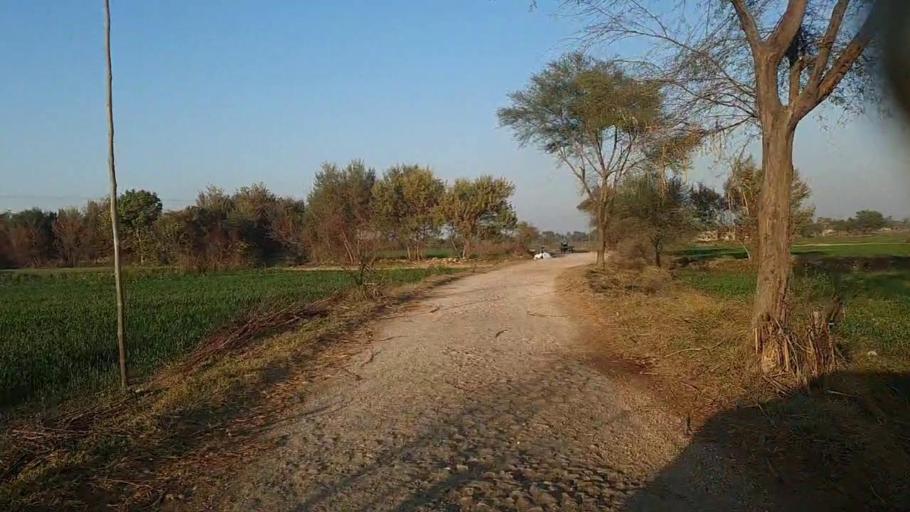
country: PK
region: Sindh
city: Mirpur Mathelo
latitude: 27.8804
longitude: 69.6510
